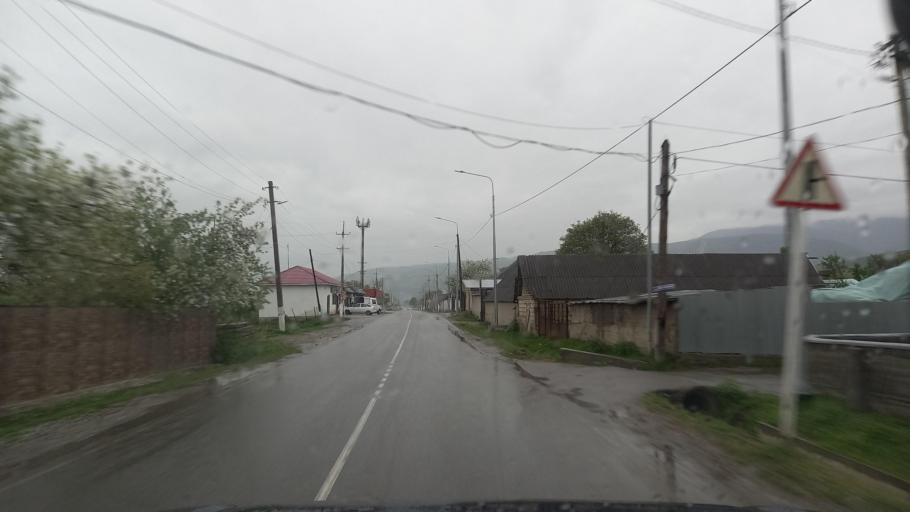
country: RU
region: Kabardino-Balkariya
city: Gundelen
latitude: 43.5899
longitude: 43.1962
